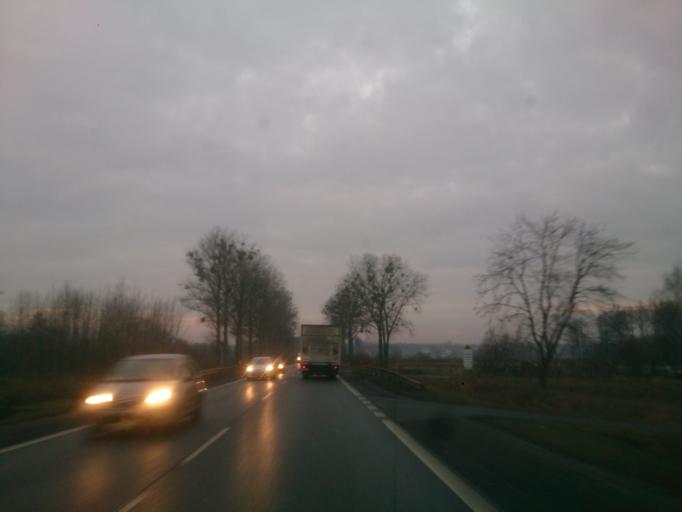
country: PL
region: Kujawsko-Pomorskie
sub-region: Grudziadz
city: Grudziadz
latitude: 53.4963
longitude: 18.6939
